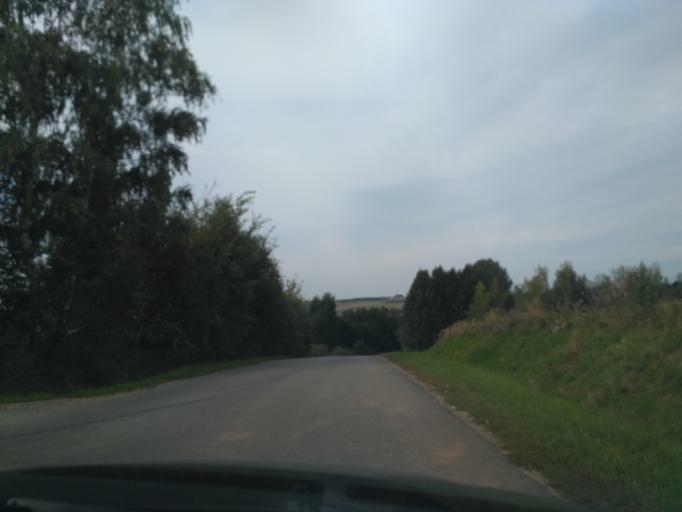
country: PL
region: Subcarpathian Voivodeship
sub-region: Powiat rzeszowski
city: Zglobien
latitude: 50.0256
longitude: 21.8437
